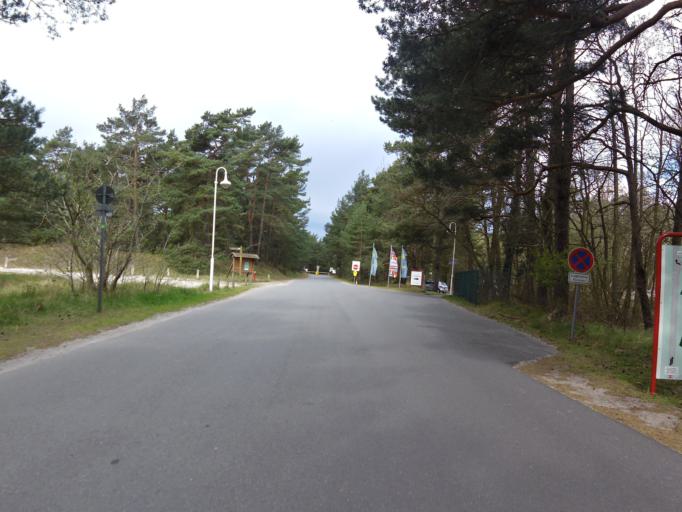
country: DE
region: Mecklenburg-Vorpommern
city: Ostseebad Prerow
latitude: 54.4539
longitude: 12.5485
